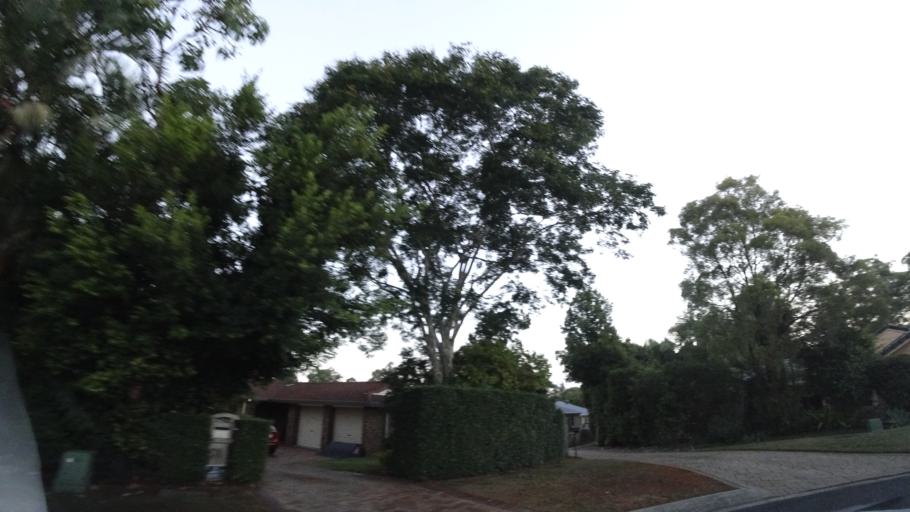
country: AU
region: Queensland
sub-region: Moreton Bay
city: Ferny Hills
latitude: -27.4056
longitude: 152.9246
